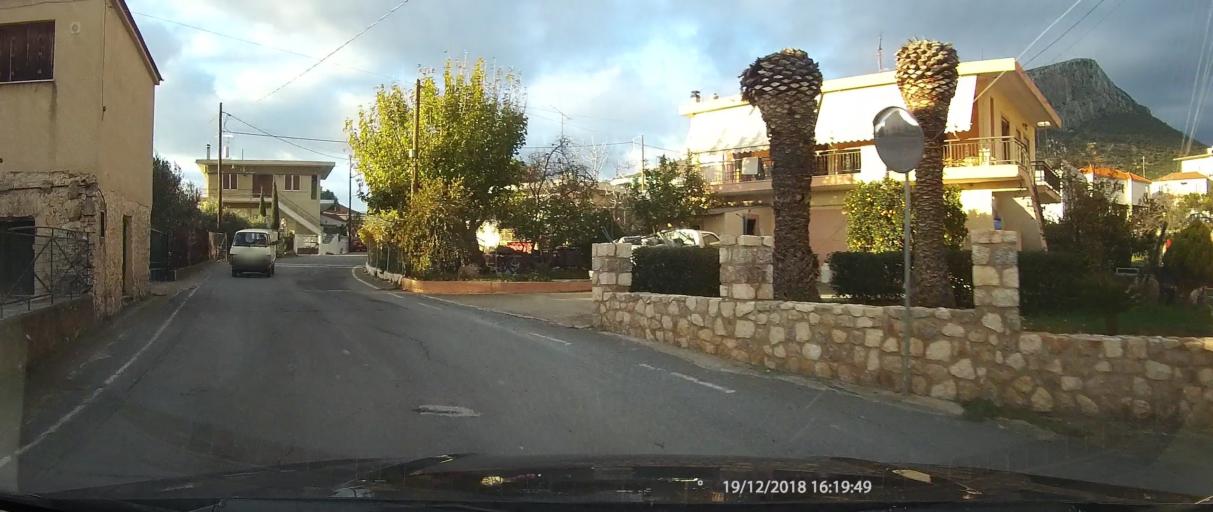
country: GR
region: Peloponnese
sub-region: Nomos Lakonias
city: Kato Glikovrisi
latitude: 36.9340
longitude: 22.8206
